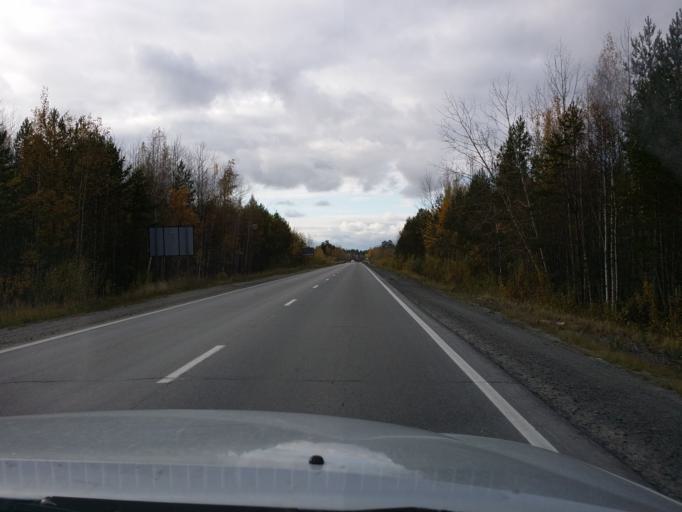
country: RU
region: Khanty-Mansiyskiy Avtonomnyy Okrug
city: Langepas
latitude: 61.2041
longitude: 75.3911
